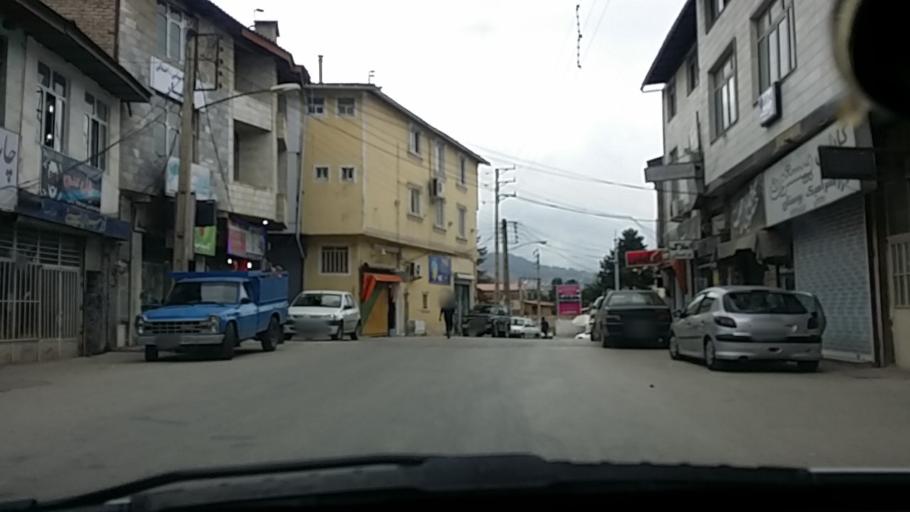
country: IR
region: Mazandaran
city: `Abbasabad
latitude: 36.5054
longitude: 51.1607
